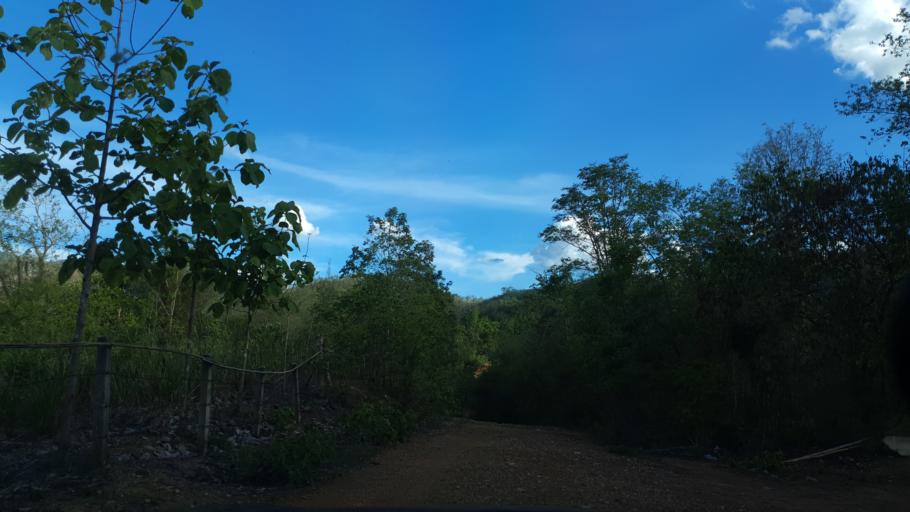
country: TH
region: Lampang
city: Sop Prap
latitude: 17.8548
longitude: 99.2836
